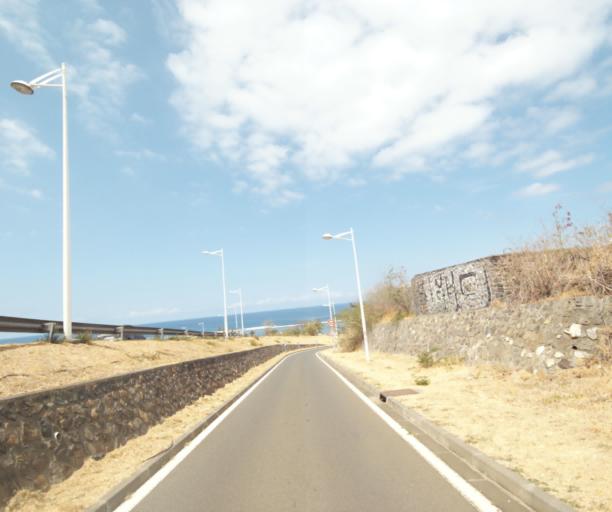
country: RE
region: Reunion
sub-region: Reunion
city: Trois-Bassins
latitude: -21.1016
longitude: 55.2480
